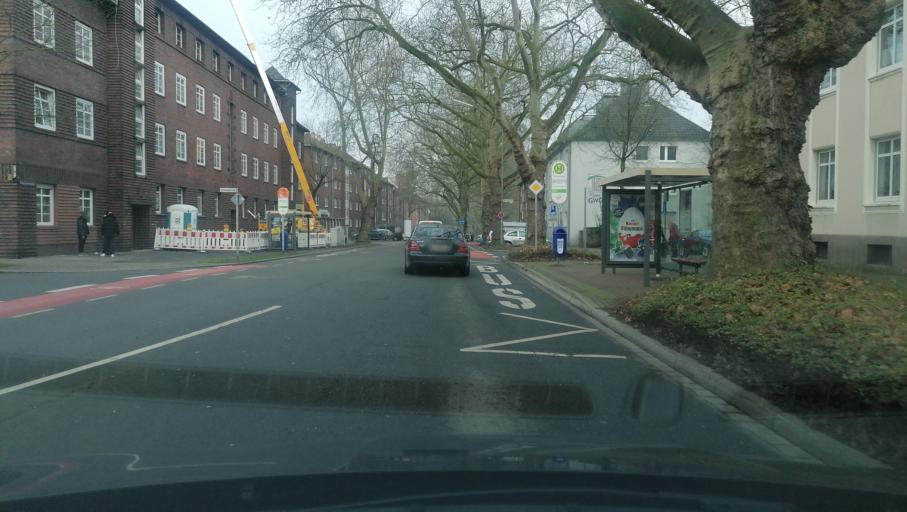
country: DE
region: North Rhine-Westphalia
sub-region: Regierungsbezirk Munster
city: Gelsenkirchen
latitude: 51.5197
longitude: 7.1073
